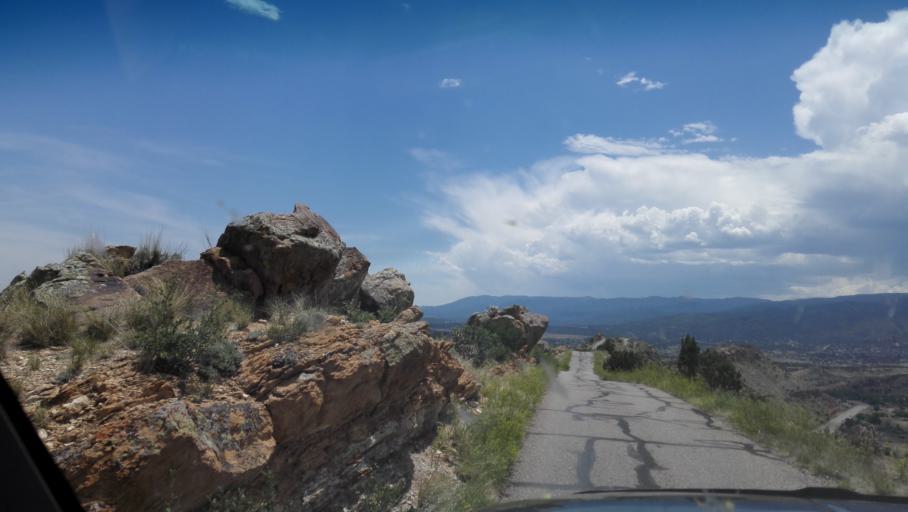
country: US
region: Colorado
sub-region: Fremont County
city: Canon City
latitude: 38.4580
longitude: -105.2505
